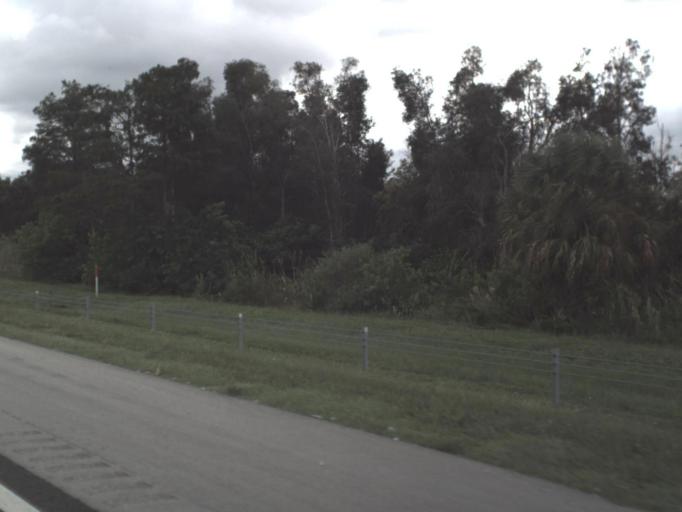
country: US
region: Florida
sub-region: Palm Beach County
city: Schall Circle
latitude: 26.7471
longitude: -80.1347
